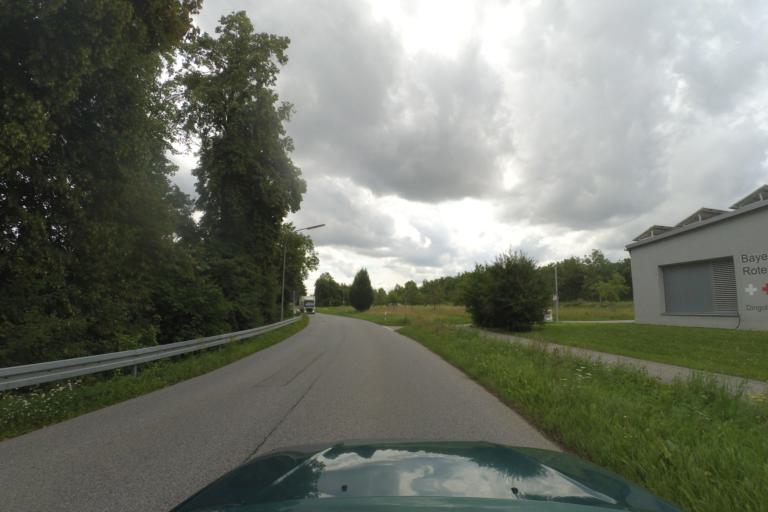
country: DE
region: Bavaria
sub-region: Lower Bavaria
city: Dingolfing
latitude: 48.6198
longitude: 12.4892
